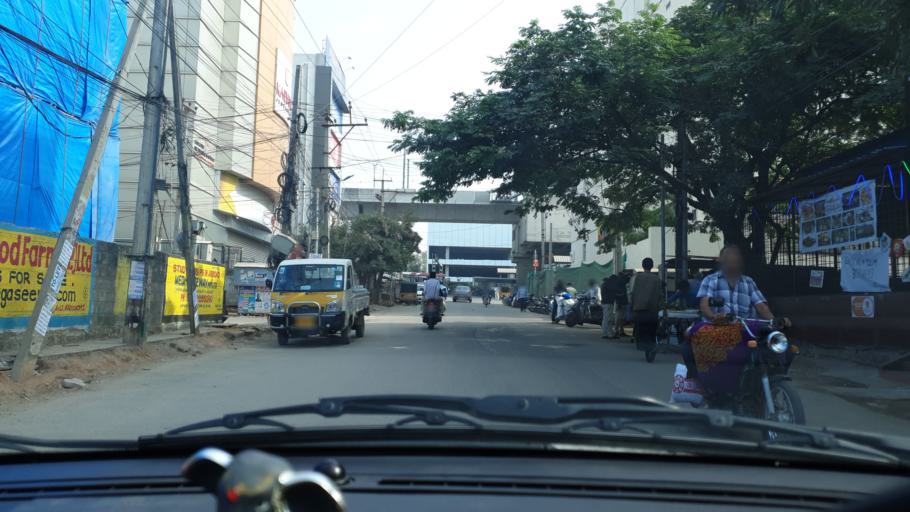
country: IN
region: Telangana
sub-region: Rangareddi
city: Kukatpalli
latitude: 17.4852
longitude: 78.4104
